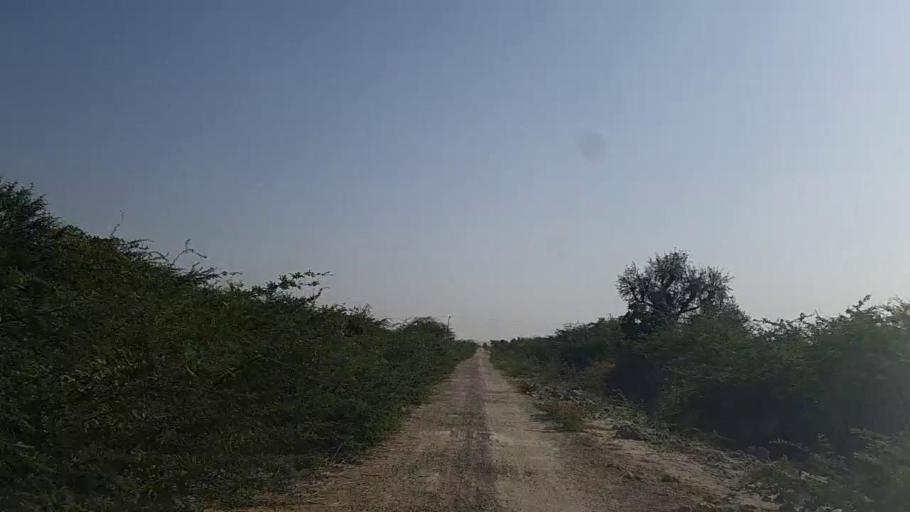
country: PK
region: Sindh
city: Kadhan
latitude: 24.5818
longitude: 69.2628
